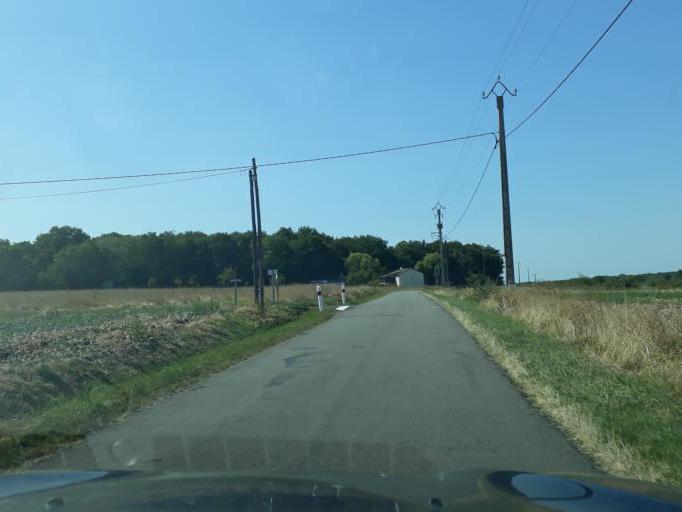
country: FR
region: Centre
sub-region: Departement du Loir-et-Cher
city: Gievres
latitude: 47.2580
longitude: 1.6965
